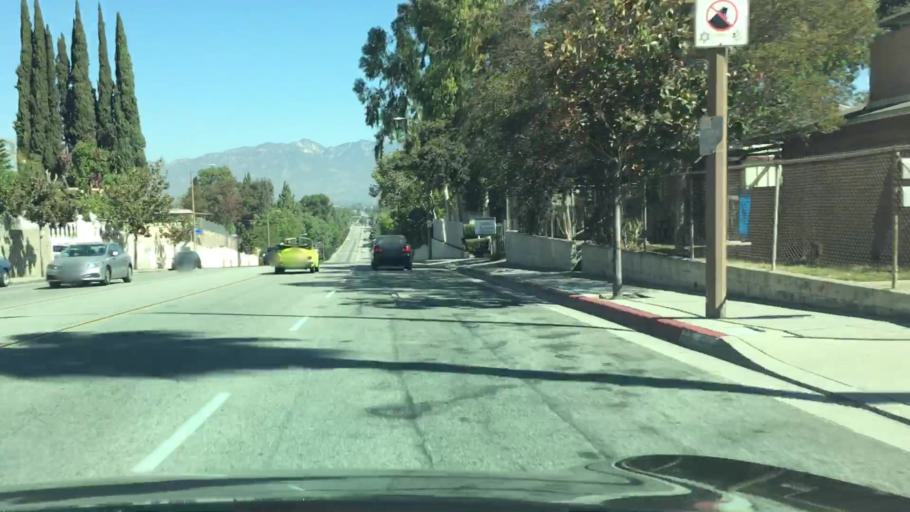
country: US
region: California
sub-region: Los Angeles County
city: South San Gabriel
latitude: 34.0424
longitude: -118.0818
